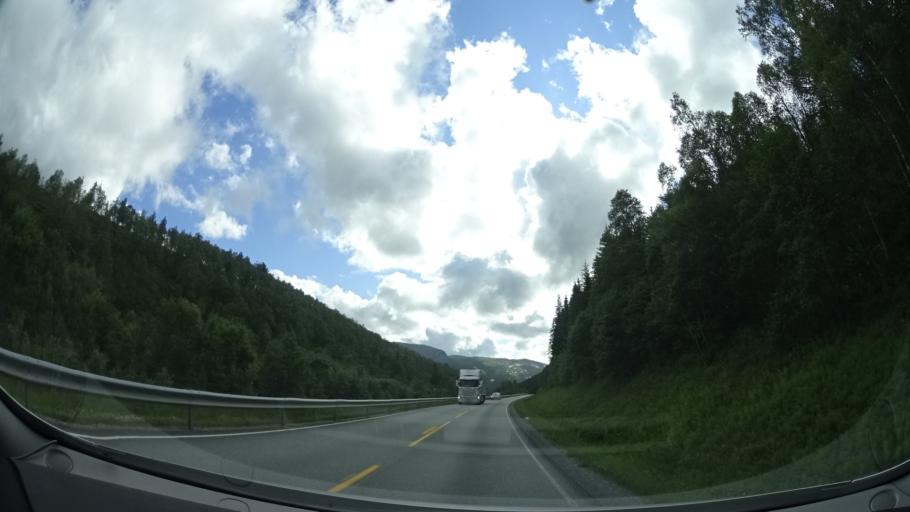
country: NO
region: Sor-Trondelag
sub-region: Hemne
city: Kyrksaeterora
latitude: 63.2156
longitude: 9.1951
